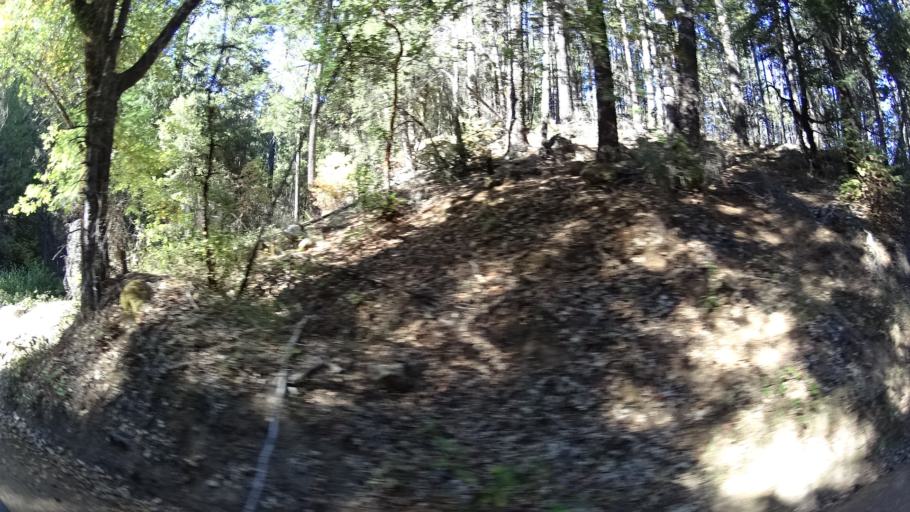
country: US
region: California
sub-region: Siskiyou County
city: Happy Camp
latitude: 41.2942
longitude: -123.2332
